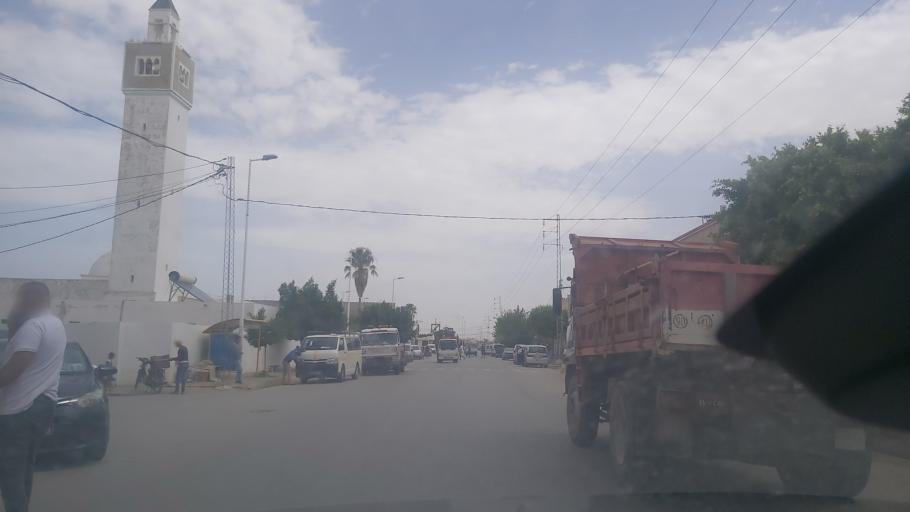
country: TN
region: Silyanah
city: Bu `Aradah
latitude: 36.3510
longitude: 9.6217
